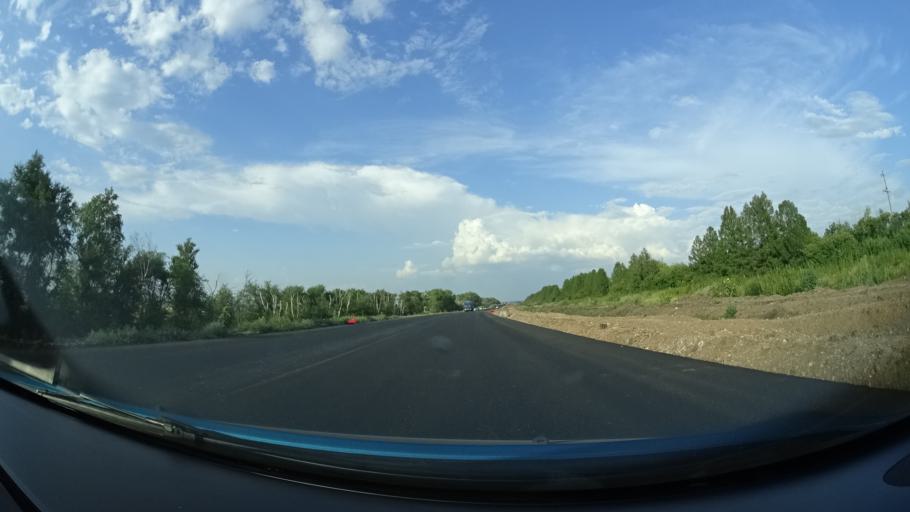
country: RU
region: Samara
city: Sukhodol
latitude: 53.7750
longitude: 50.9019
